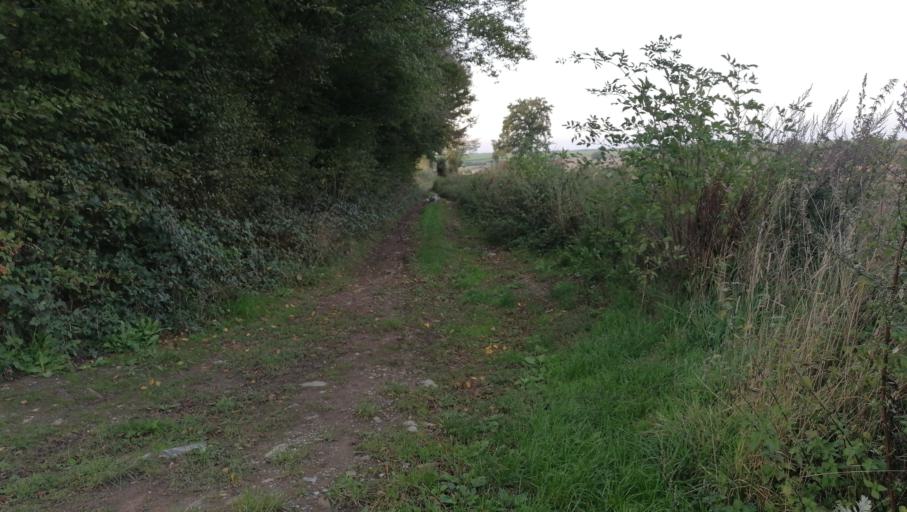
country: FR
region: Nord-Pas-de-Calais
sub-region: Departement du Nord
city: Recquignies
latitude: 50.2333
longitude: 4.0519
